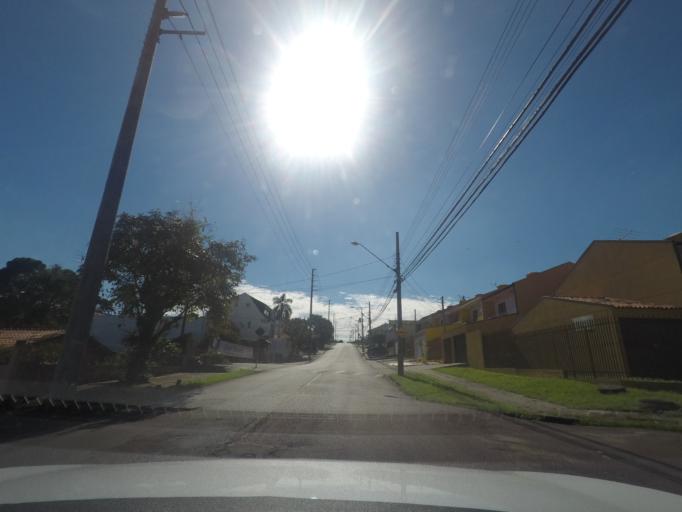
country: BR
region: Parana
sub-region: Sao Jose Dos Pinhais
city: Sao Jose dos Pinhais
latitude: -25.5046
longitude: -49.2775
